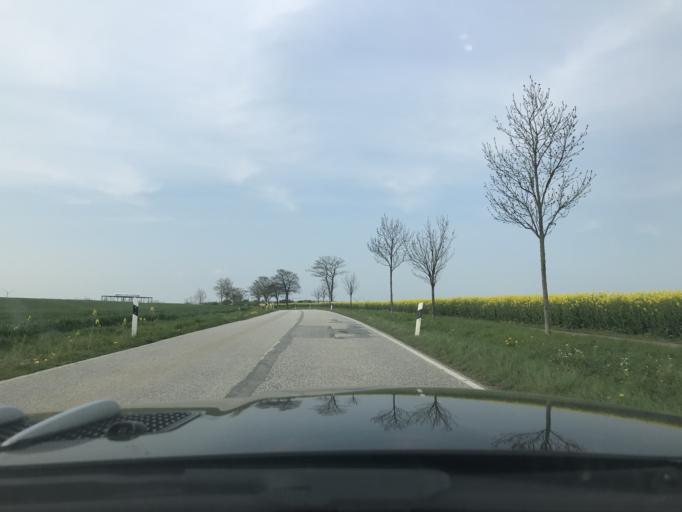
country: DE
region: Schleswig-Holstein
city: Heringsdorf
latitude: 54.3082
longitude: 11.0086
